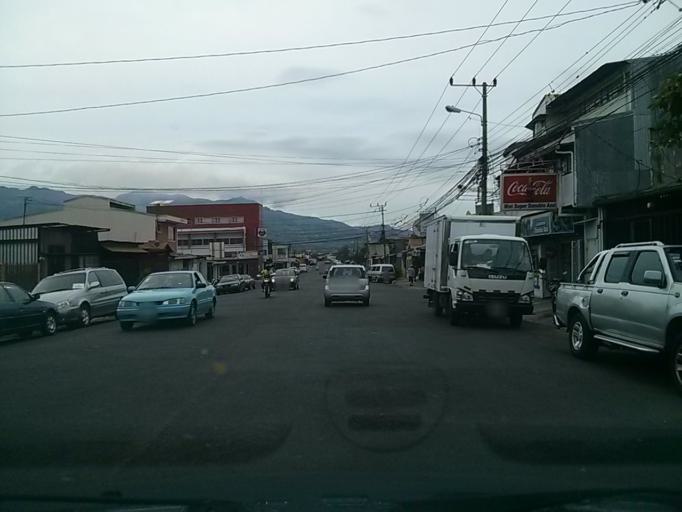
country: CR
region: San Jose
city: Patarra
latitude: 9.8927
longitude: -84.0491
